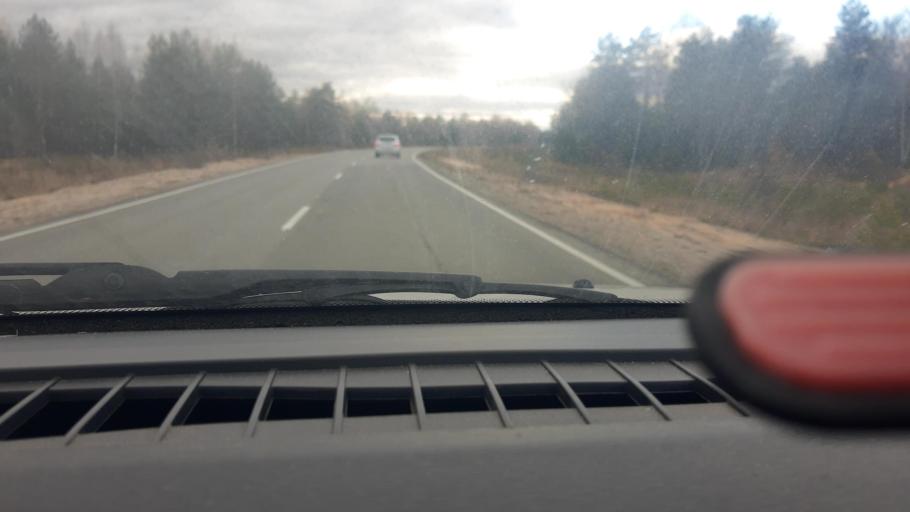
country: RU
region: Nizjnij Novgorod
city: Babino
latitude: 56.2969
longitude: 43.6461
